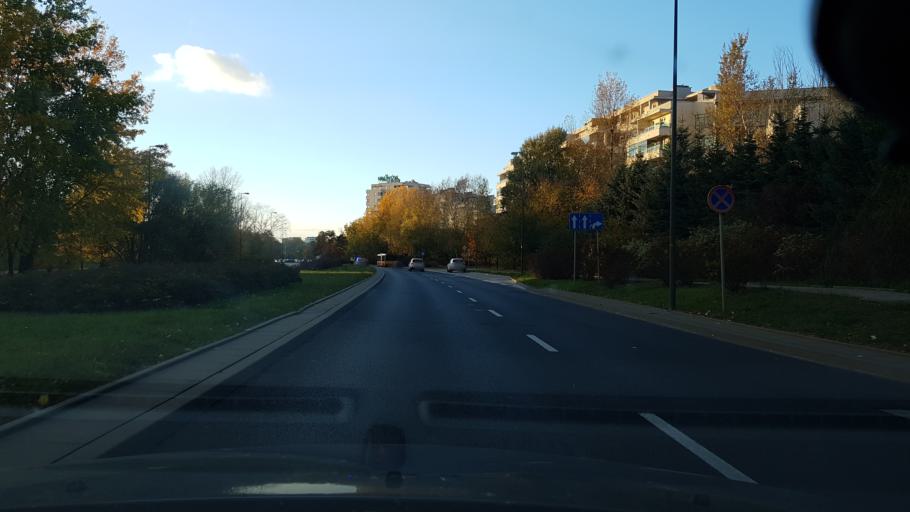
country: PL
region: Masovian Voivodeship
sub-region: Warszawa
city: Ursynow
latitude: 52.1533
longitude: 21.0554
